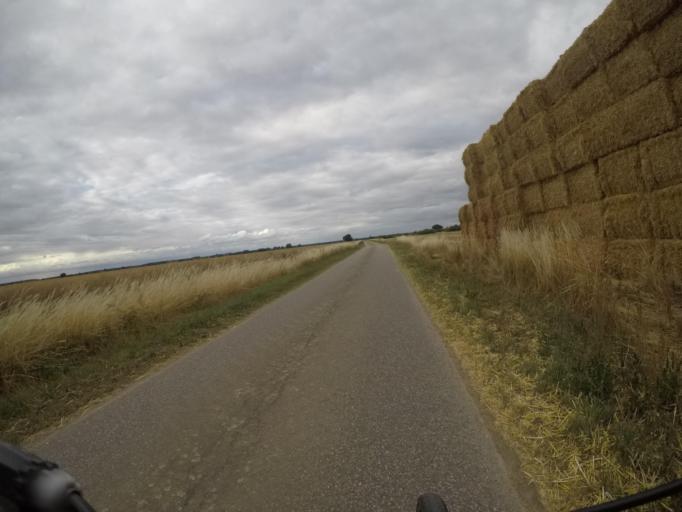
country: DE
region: Lower Saxony
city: Neu Darchau
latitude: 53.2423
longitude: 10.9057
